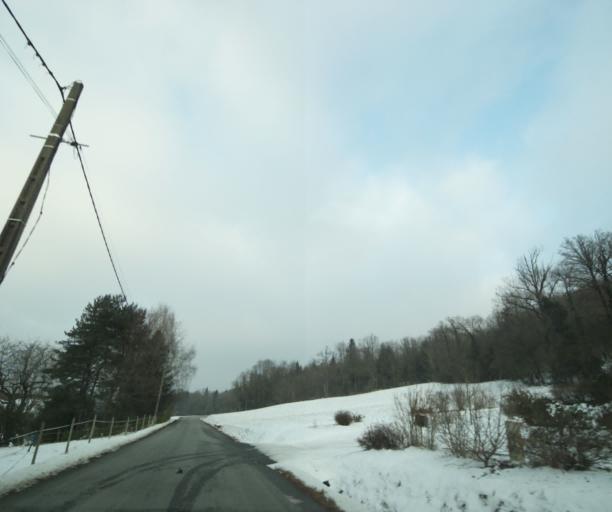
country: FR
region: Rhone-Alpes
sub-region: Departement de la Haute-Savoie
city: Monnetier-Mornex
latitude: 46.1370
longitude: 6.2236
